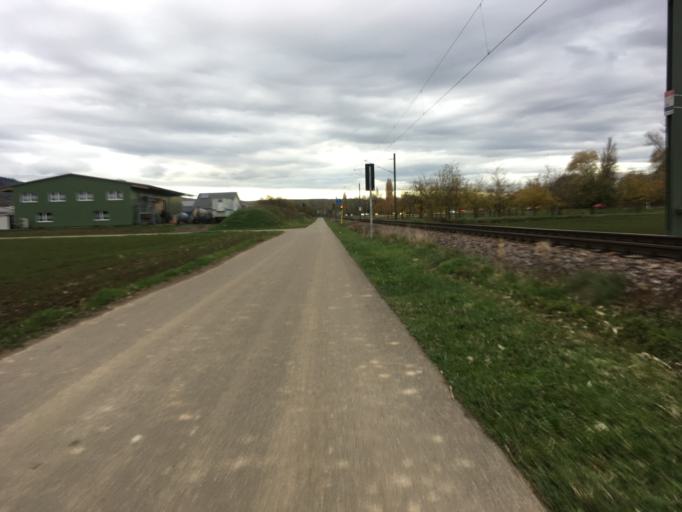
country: DE
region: Baden-Wuerttemberg
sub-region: Freiburg Region
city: Gottenheim
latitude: 48.0591
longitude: 7.7237
